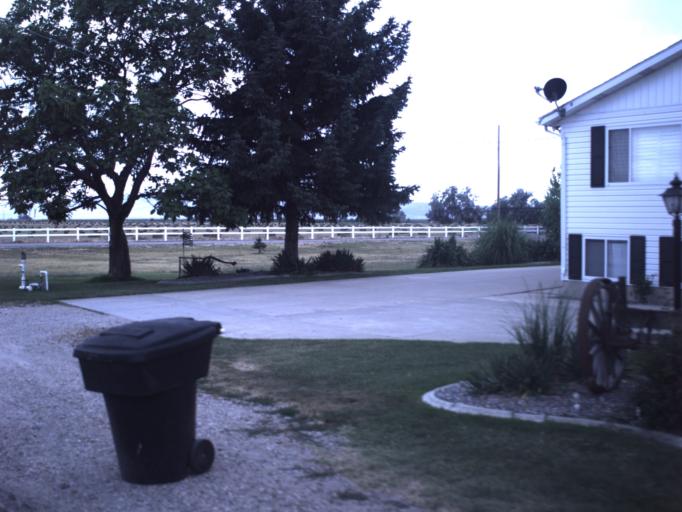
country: US
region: Utah
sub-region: Davis County
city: West Point
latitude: 41.0970
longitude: -112.1127
